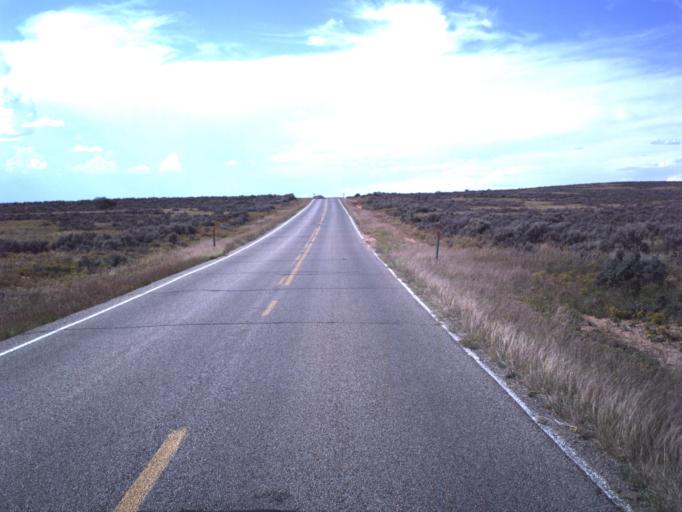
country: US
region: Utah
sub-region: Grand County
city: Moab
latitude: 38.5249
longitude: -109.7442
